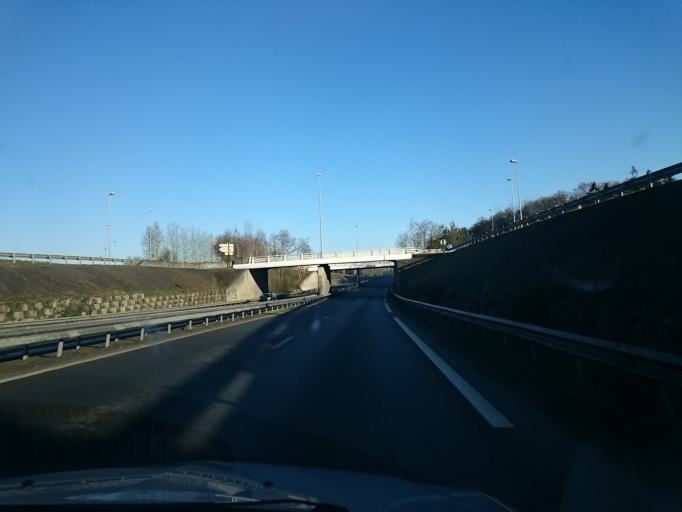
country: FR
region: Brittany
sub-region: Departement d'Ille-et-Vilaine
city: Vern-sur-Seiche
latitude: 48.0626
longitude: -1.6172
